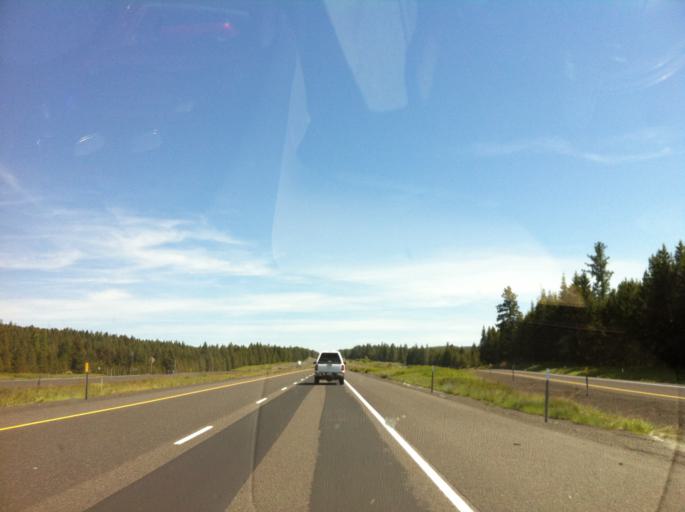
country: US
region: Oregon
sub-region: Umatilla County
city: Mission
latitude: 45.5111
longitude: -118.4304
